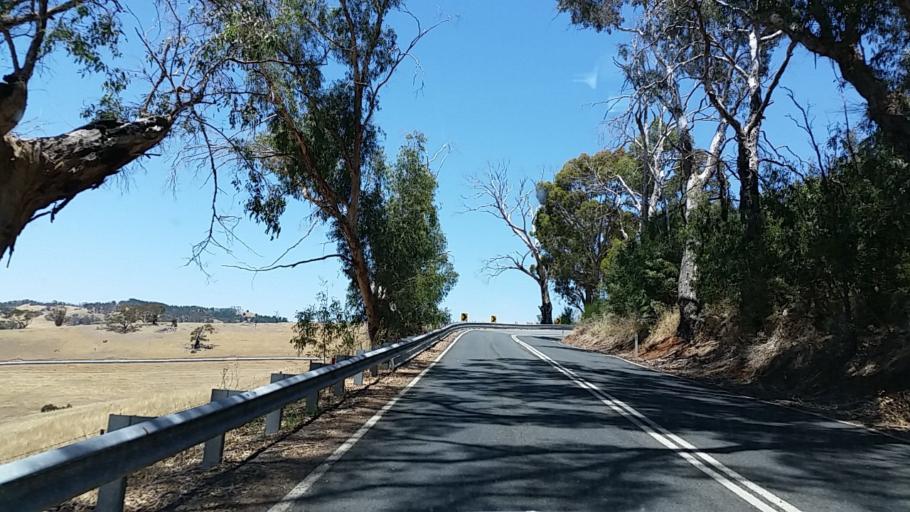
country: AU
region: South Australia
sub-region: Adelaide Hills
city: Gumeracha
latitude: -34.8234
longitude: 138.8430
